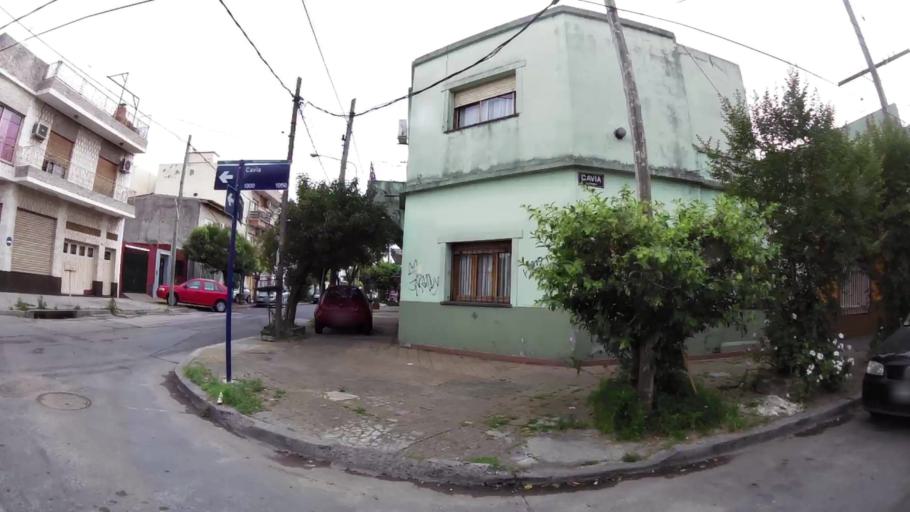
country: AR
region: Buenos Aires
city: San Justo
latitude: -34.6609
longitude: -58.5238
